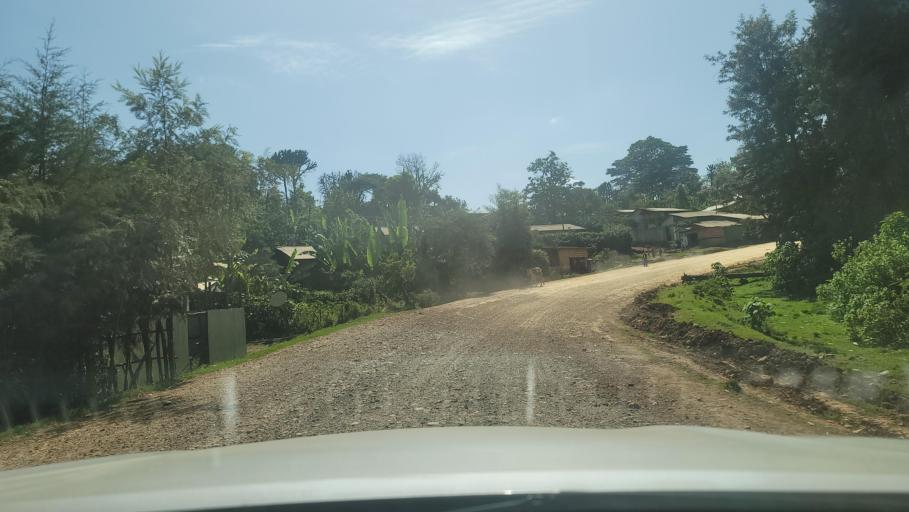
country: ET
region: Oromiya
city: Agaro
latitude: 7.7866
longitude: 36.4250
